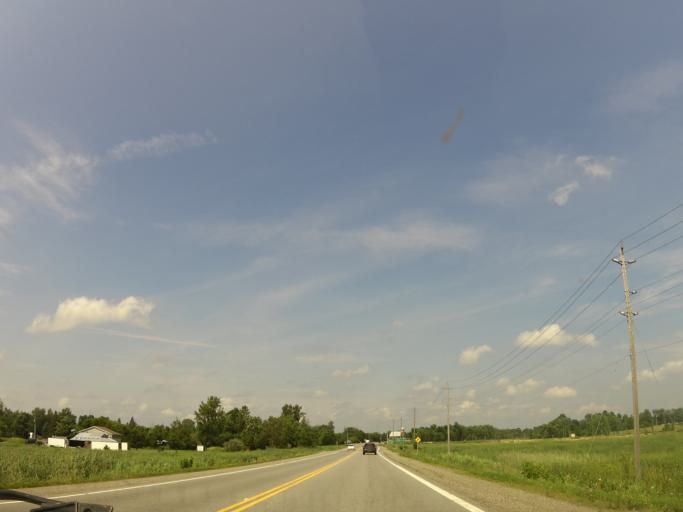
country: CA
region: Ontario
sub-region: Lanark County
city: Smiths Falls
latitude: 44.8201
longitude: -76.0915
